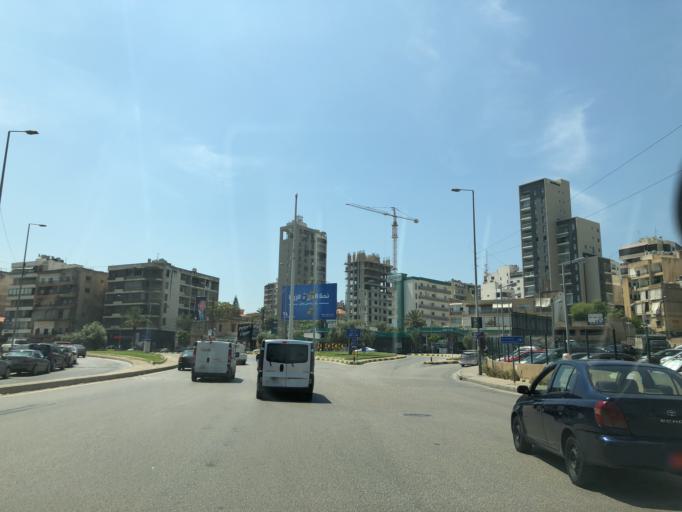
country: LB
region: Mont-Liban
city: Jdaidet el Matn
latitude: 33.8817
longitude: 35.5407
